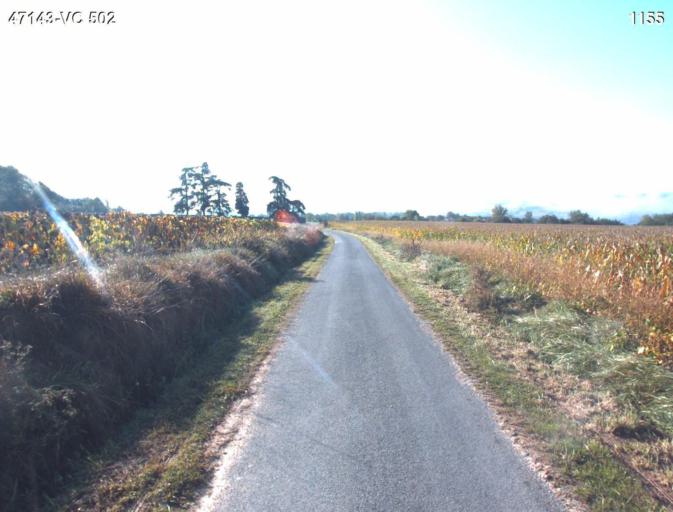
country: FR
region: Aquitaine
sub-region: Departement du Lot-et-Garonne
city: Vianne
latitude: 44.1738
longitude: 0.3266
